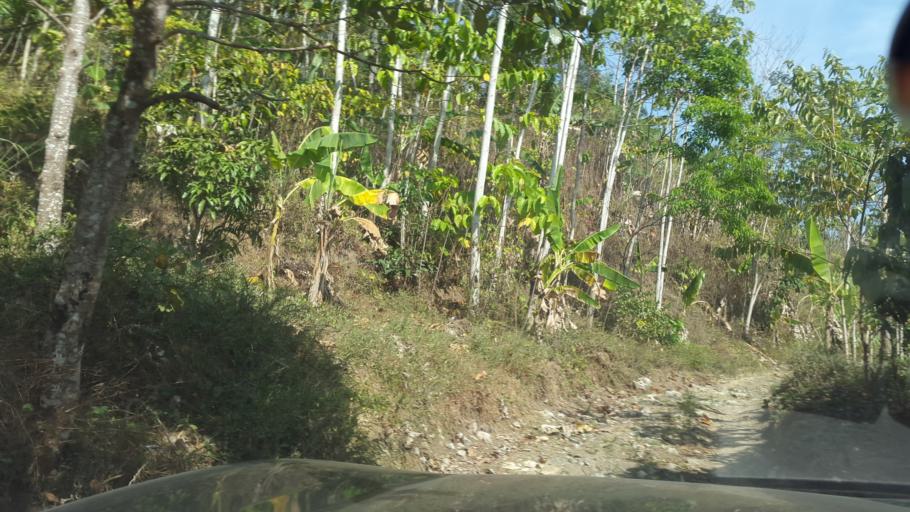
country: ID
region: West Java
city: Bojonggaling
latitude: -6.9273
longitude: 106.6332
